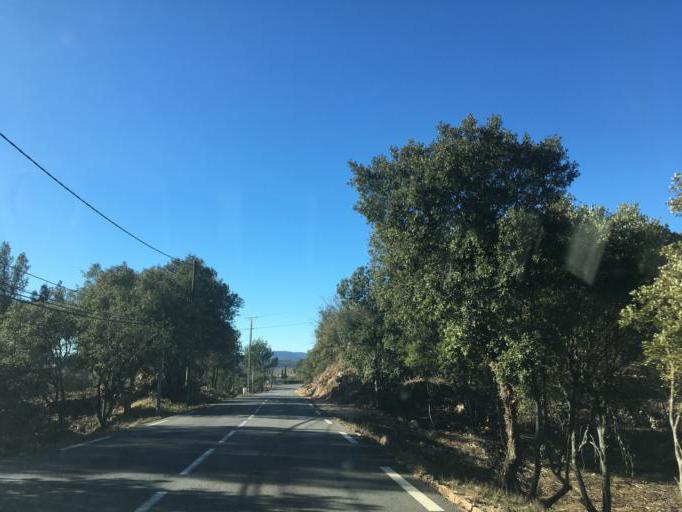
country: FR
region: Provence-Alpes-Cote d'Azur
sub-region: Departement du Var
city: Barjols
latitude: 43.5951
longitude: 6.0319
